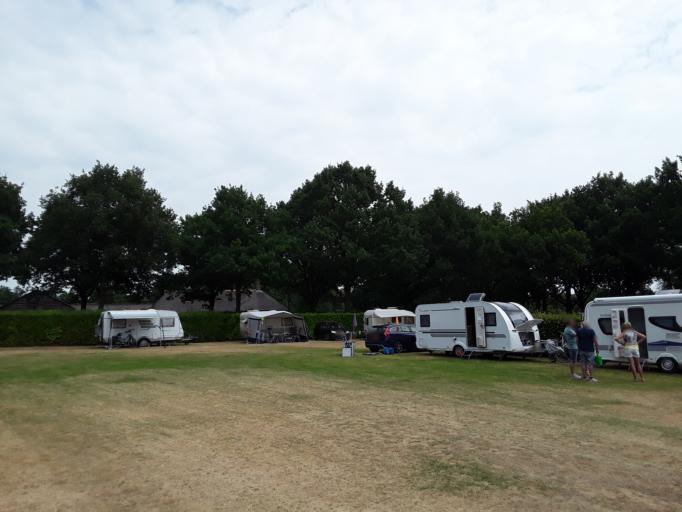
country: NL
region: Gelderland
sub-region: Gemeente Rheden
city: De Steeg
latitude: 52.0175
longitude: 6.0631
